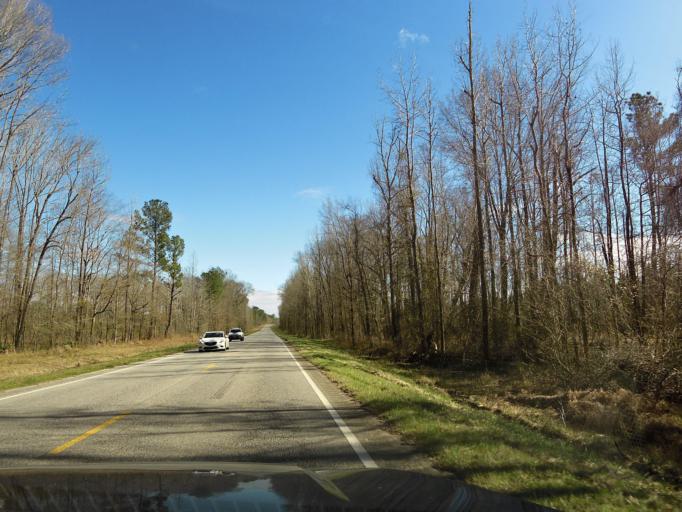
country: US
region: Alabama
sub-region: Barbour County
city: Clayton
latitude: 32.0440
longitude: -85.4243
